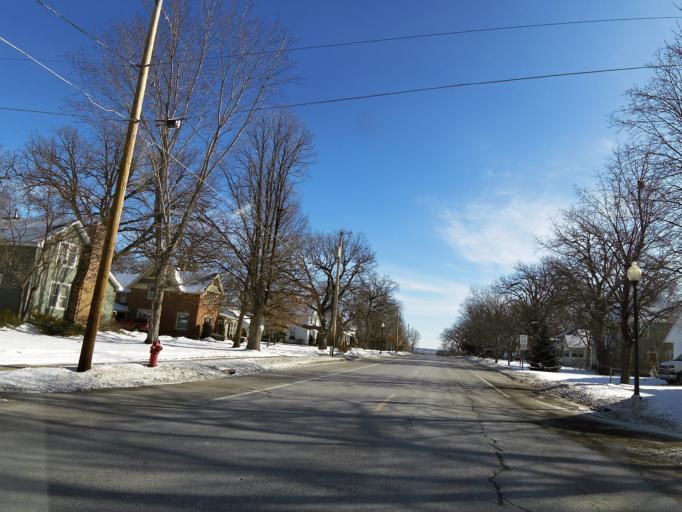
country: US
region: Minnesota
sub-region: Dakota County
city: Hastings
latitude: 44.7442
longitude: -92.8651
